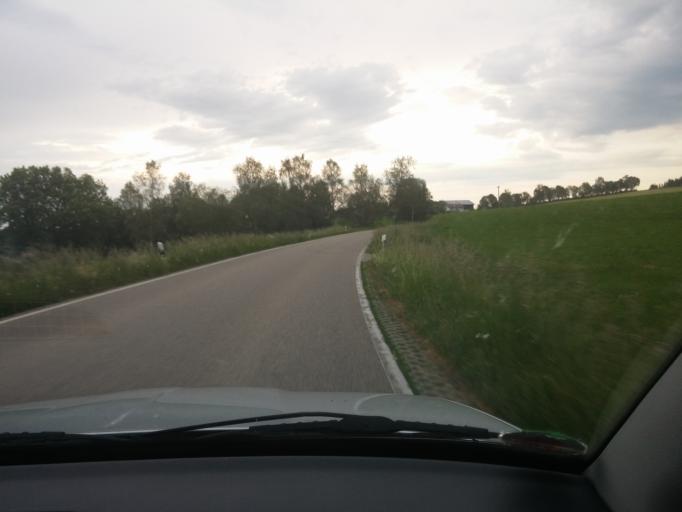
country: DE
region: Bavaria
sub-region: Swabia
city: Legau
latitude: 47.8329
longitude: 10.1026
